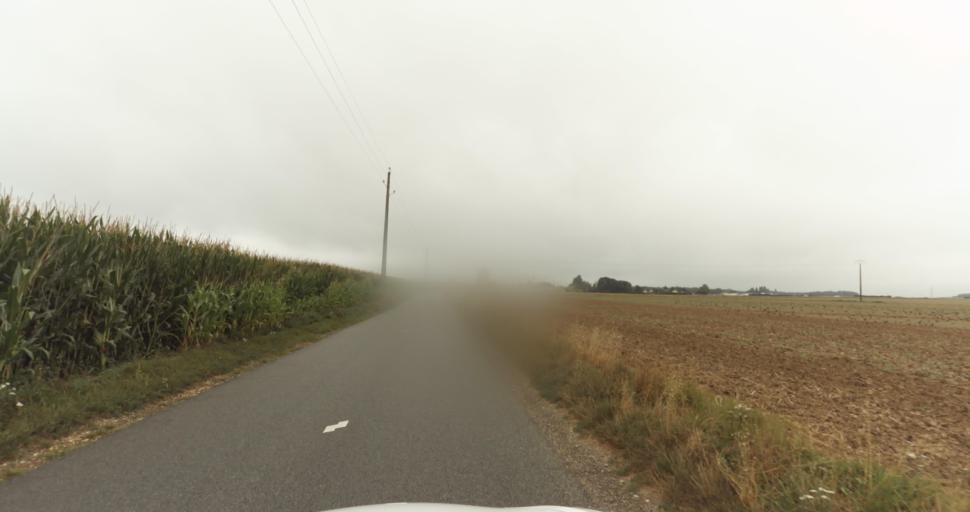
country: FR
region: Haute-Normandie
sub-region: Departement de l'Eure
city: Normanville
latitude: 49.0805
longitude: 1.1937
